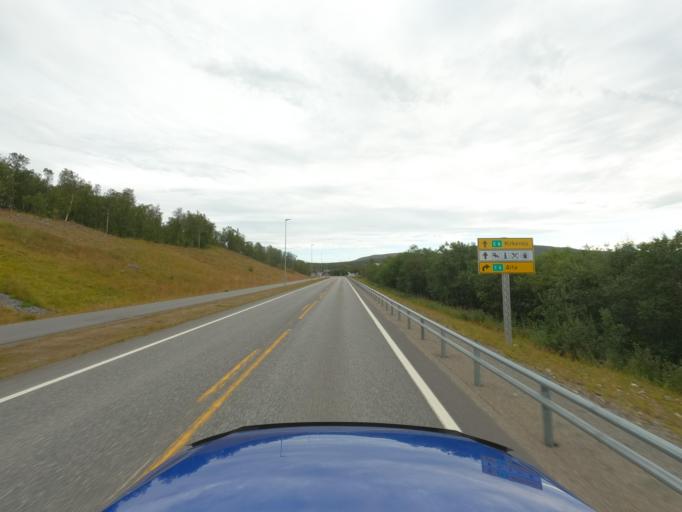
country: NO
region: Finnmark Fylke
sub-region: Kvalsund
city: Kvalsund
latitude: 70.4339
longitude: 24.4964
